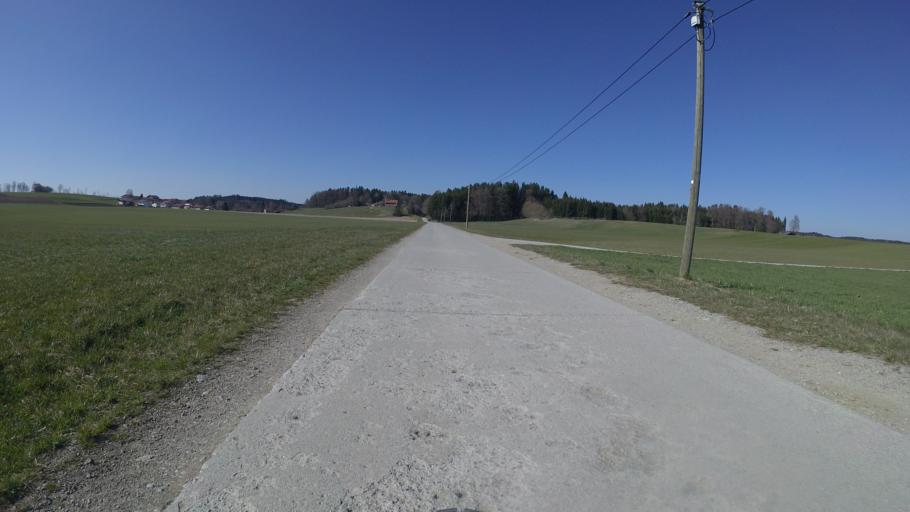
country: DE
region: Bavaria
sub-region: Upper Bavaria
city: Seeon-Seebruck
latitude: 47.9558
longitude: 12.5149
